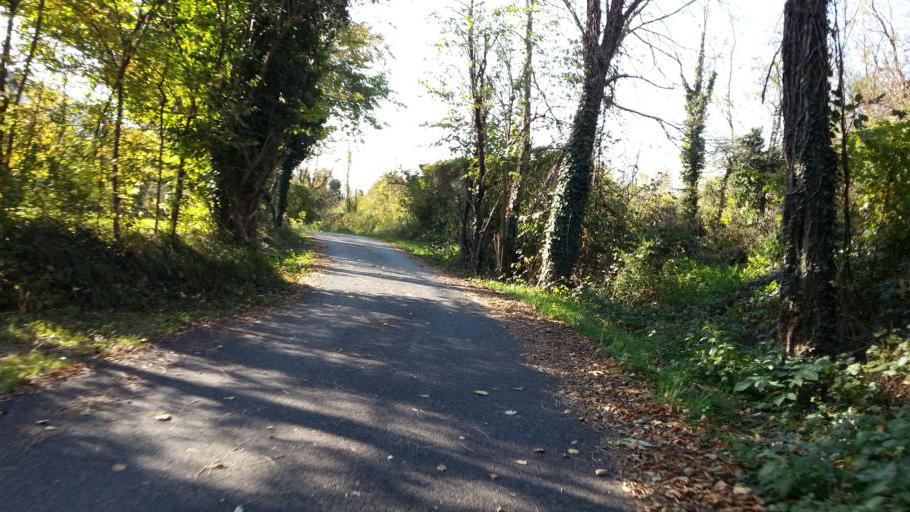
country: IT
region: Friuli Venezia Giulia
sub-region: Provincia di Udine
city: Venzone
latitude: 46.3238
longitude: 13.1281
